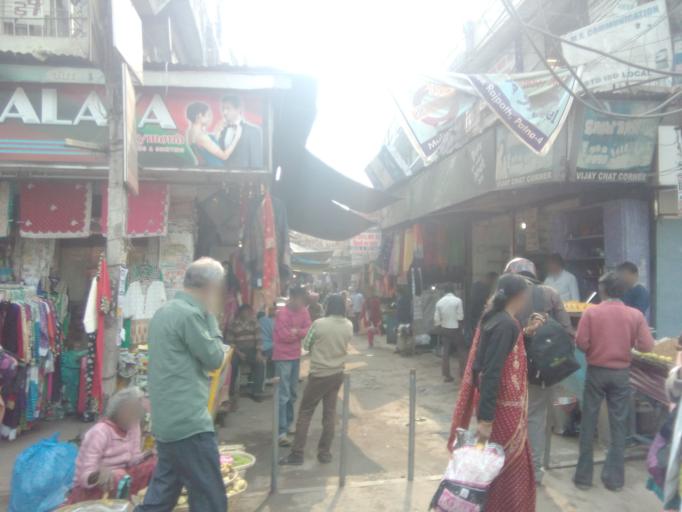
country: IN
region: Bihar
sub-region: Patna
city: Patna
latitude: 25.6197
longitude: 85.1580
